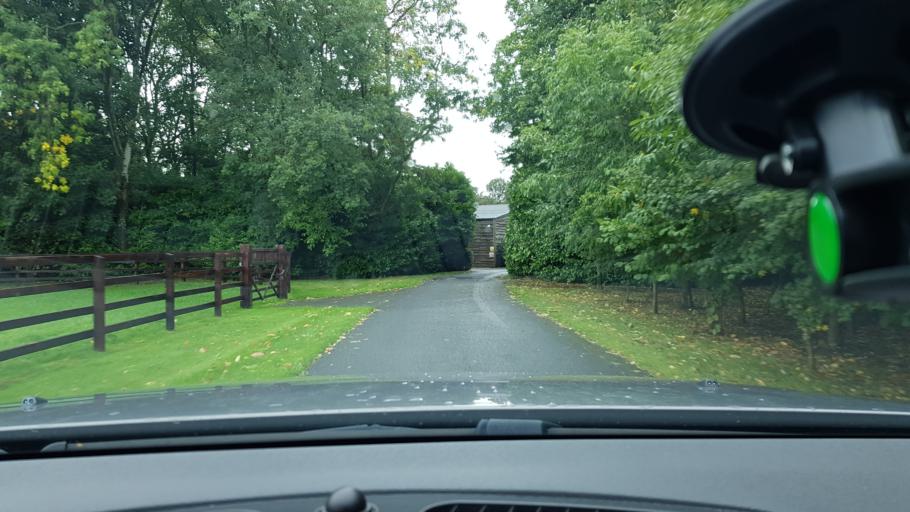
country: GB
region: England
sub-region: West Berkshire
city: Hungerford
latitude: 51.4234
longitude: -1.4818
